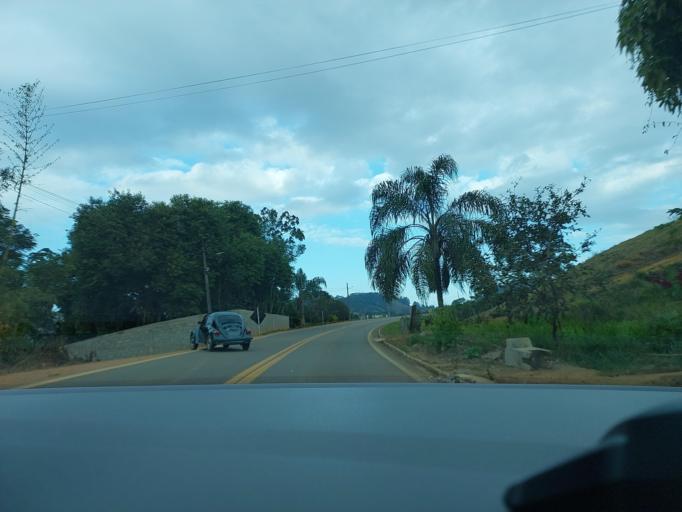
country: BR
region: Minas Gerais
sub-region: Mirai
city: Mirai
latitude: -21.0086
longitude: -42.5499
